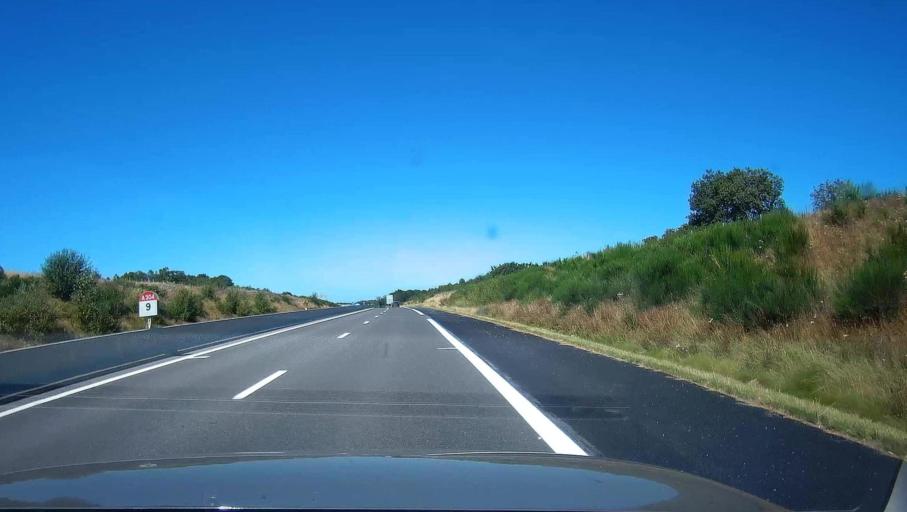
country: FR
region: Champagne-Ardenne
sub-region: Departement des Ardennes
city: Rocroi
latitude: 49.8910
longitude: 4.5202
